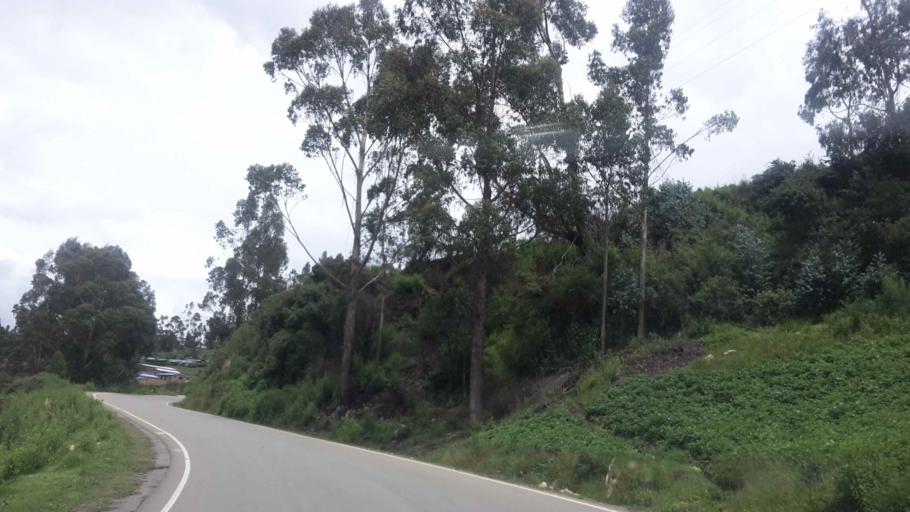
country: BO
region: Cochabamba
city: Arani
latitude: -17.4955
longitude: -65.4397
